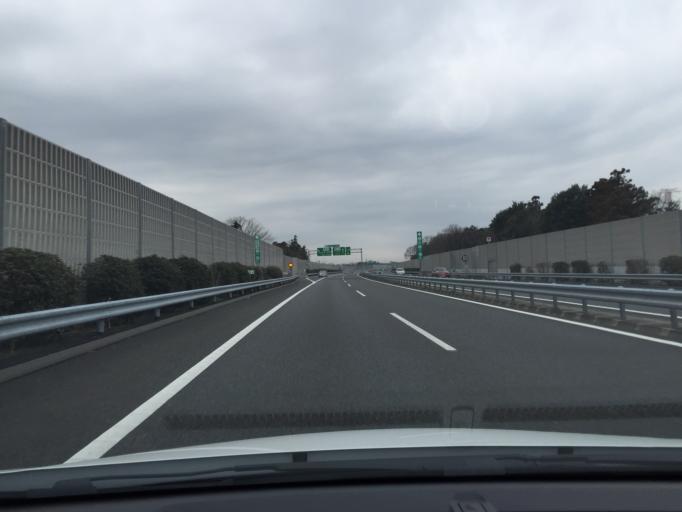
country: JP
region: Saitama
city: Sakado
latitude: 35.9395
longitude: 139.4104
